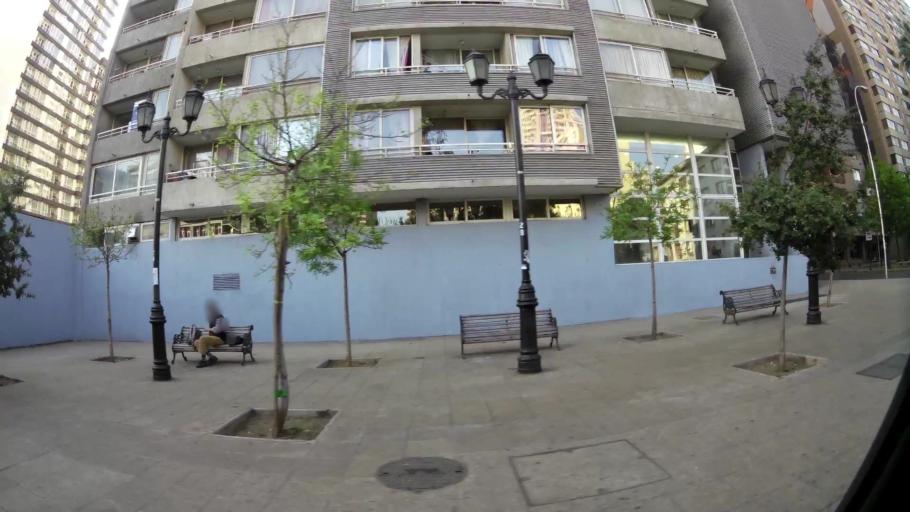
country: CL
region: Santiago Metropolitan
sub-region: Provincia de Santiago
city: Santiago
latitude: -33.4344
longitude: -70.6576
